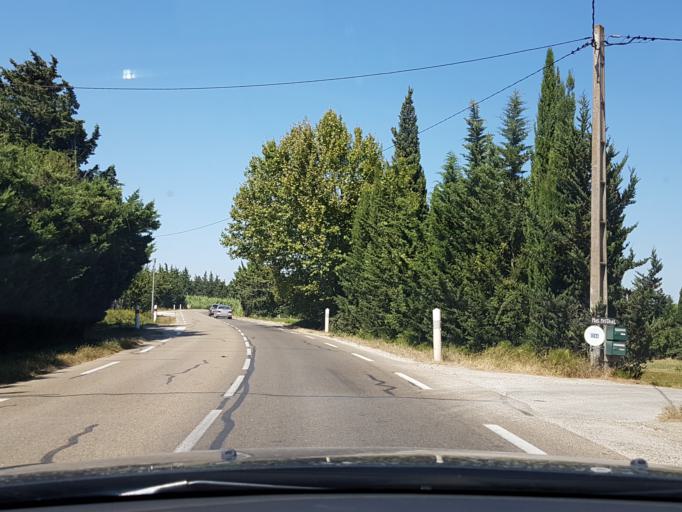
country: FR
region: Provence-Alpes-Cote d'Azur
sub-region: Departement des Bouches-du-Rhone
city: Eyragues
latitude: 43.8510
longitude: 4.8411
